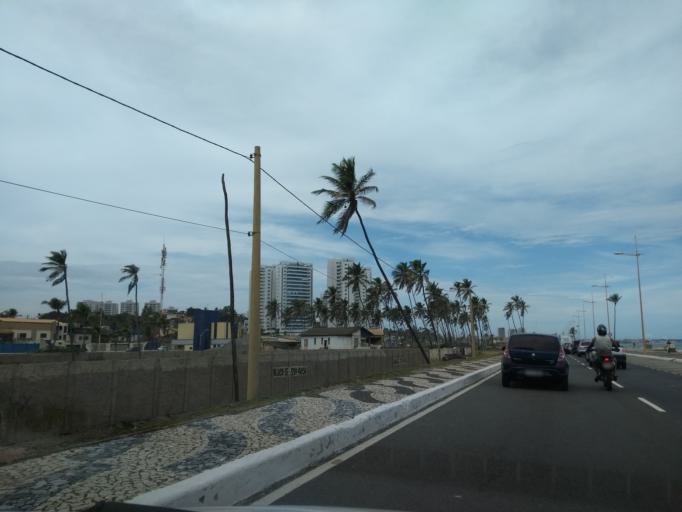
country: BR
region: Bahia
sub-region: Salvador
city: Salvador
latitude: -12.9718
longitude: -38.4122
